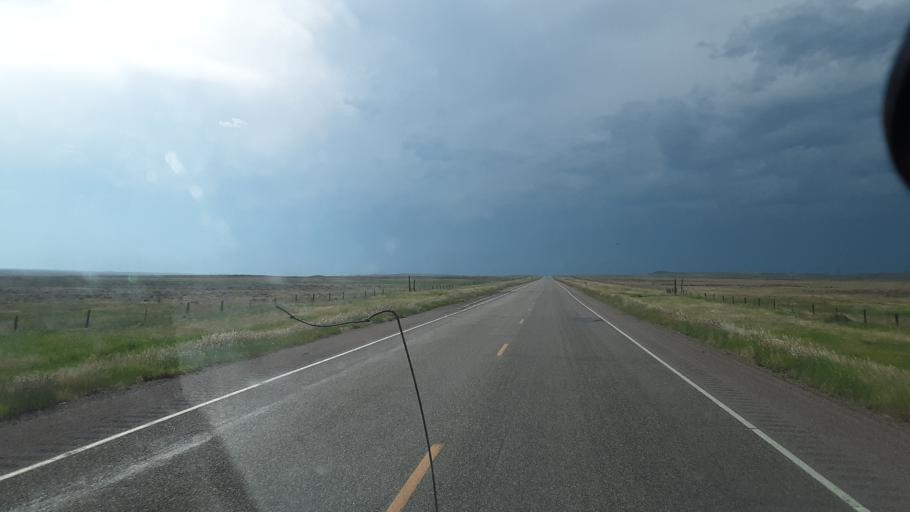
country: US
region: Montana
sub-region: Carter County
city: Ekalaka
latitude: 45.1299
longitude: -104.6705
